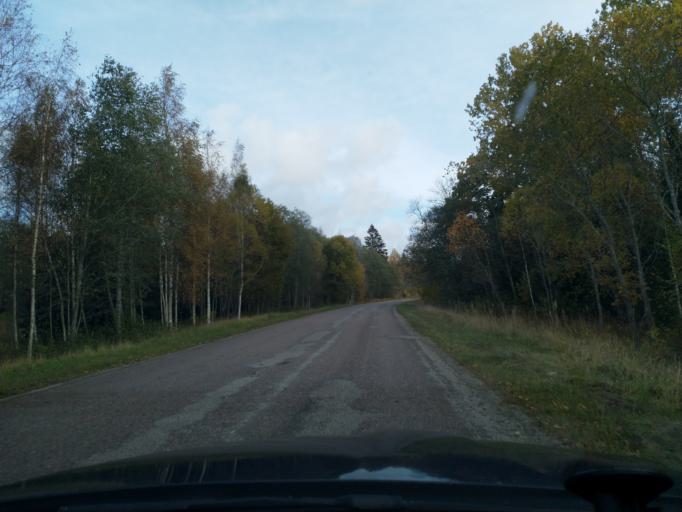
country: LV
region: Dundaga
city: Dundaga
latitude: 57.5504
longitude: 22.3566
